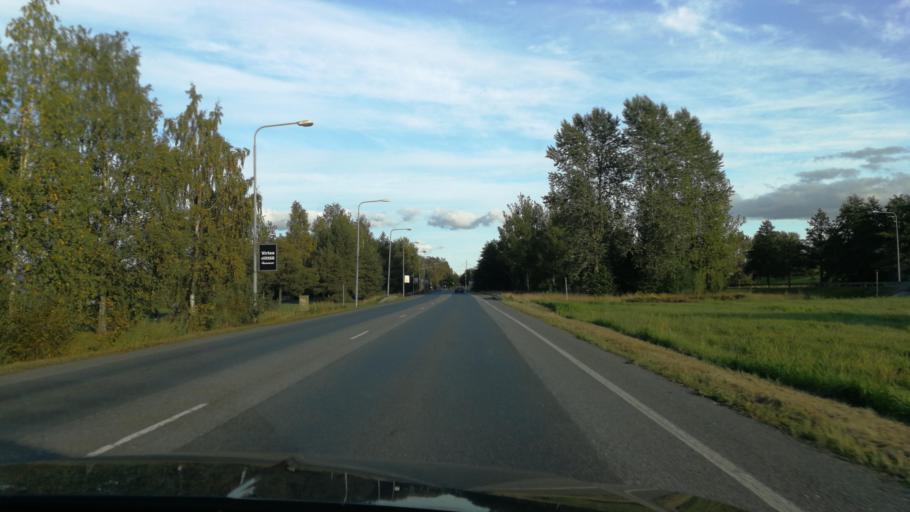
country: FI
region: Satakunta
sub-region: Pori
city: Pori
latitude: 61.4790
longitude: 21.7724
